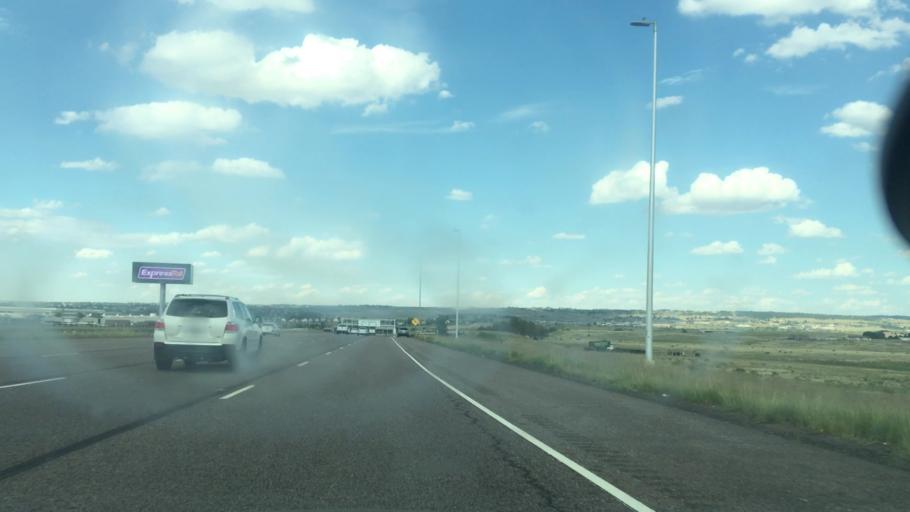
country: US
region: Colorado
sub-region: Douglas County
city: Meridian
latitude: 39.5532
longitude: -104.8346
